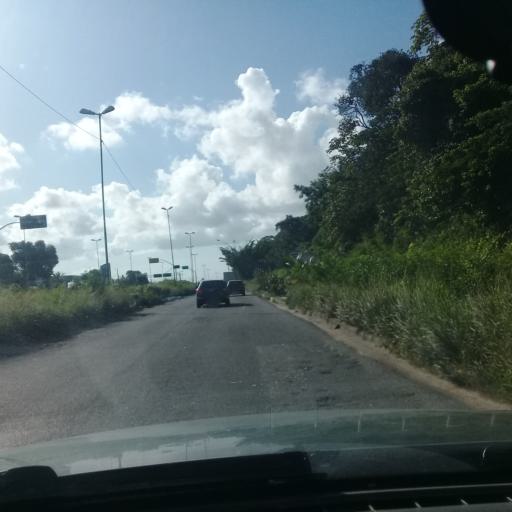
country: BR
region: Pernambuco
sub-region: Abreu E Lima
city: Abreu e Lima
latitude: -7.9248
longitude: -34.8901
